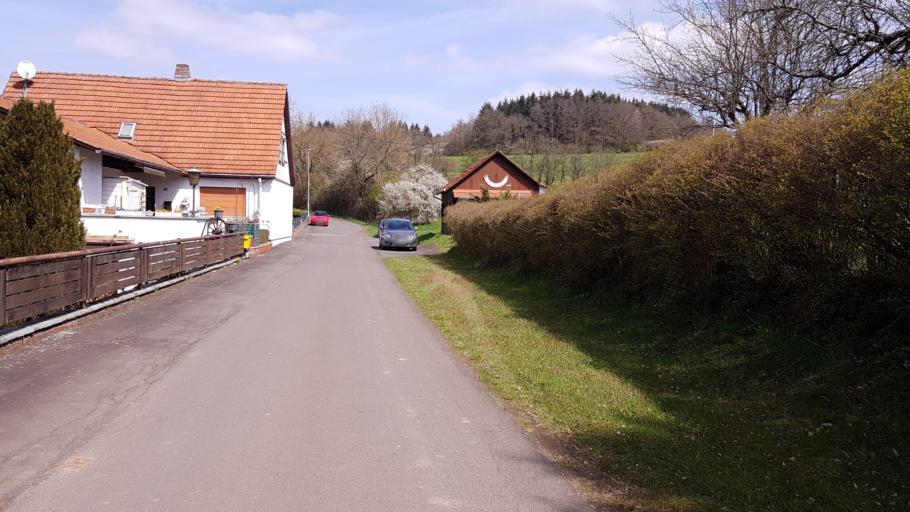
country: DE
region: Hesse
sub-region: Regierungsbezirk Giessen
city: Homberg
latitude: 50.6538
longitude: 9.0355
